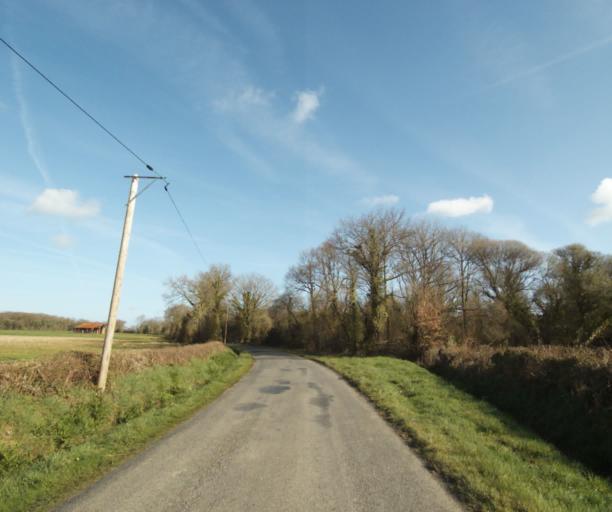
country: FR
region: Pays de la Loire
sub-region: Departement de la Loire-Atlantique
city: Bouvron
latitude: 47.3920
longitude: -1.8436
